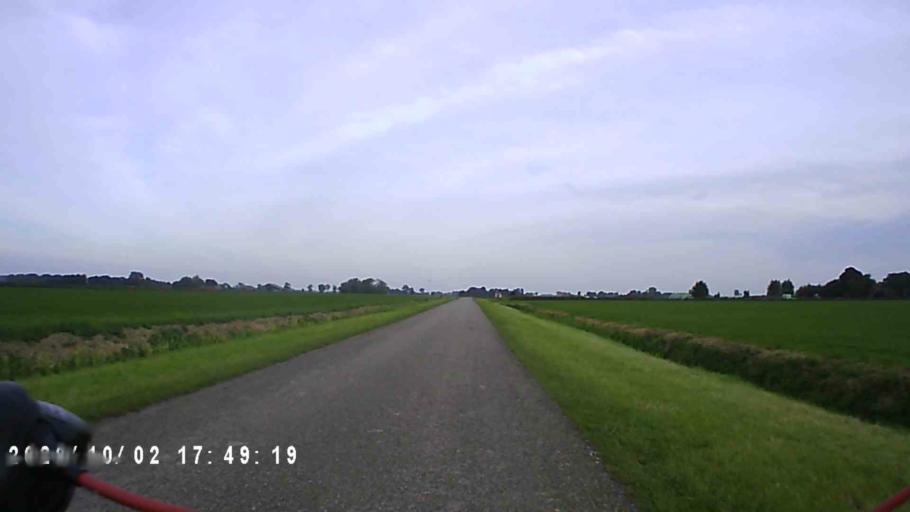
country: NL
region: Groningen
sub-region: Gemeente Zuidhorn
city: Oldehove
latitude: 53.3365
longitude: 6.4051
